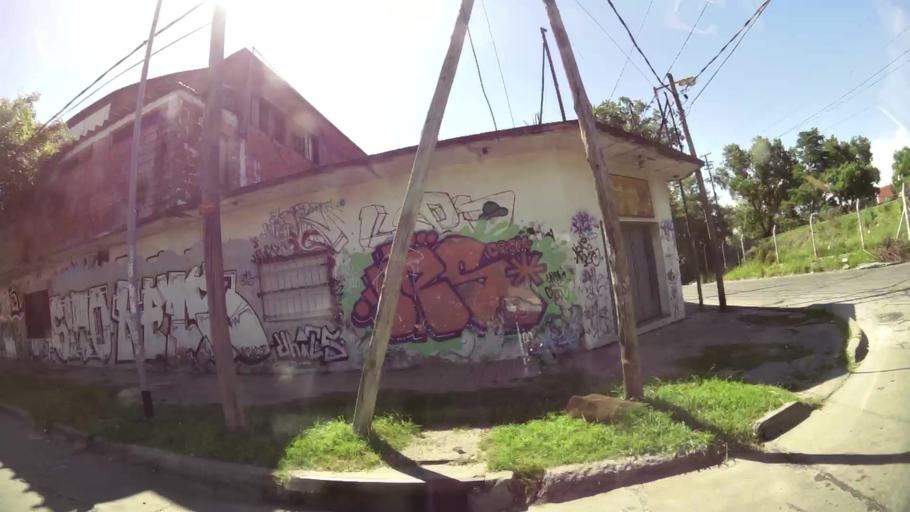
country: AR
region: Buenos Aires
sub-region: Partido de General San Martin
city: General San Martin
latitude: -34.5375
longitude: -58.5733
